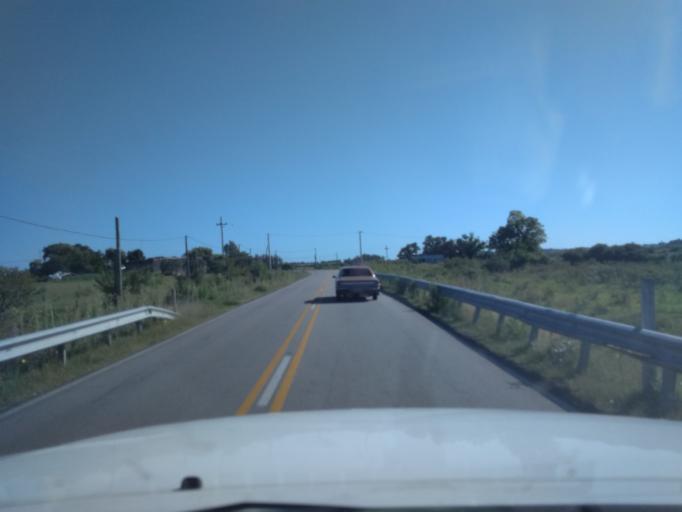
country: UY
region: Canelones
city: San Ramon
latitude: -34.3209
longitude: -55.9609
